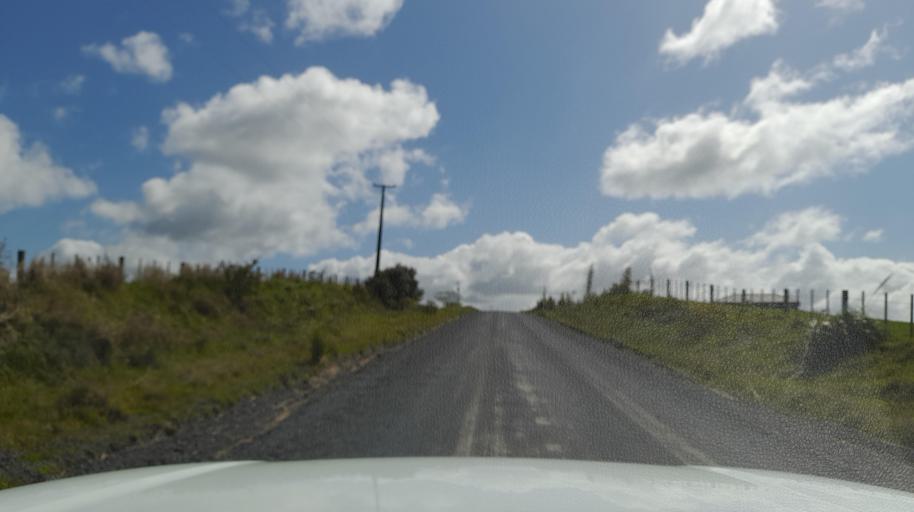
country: NZ
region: Northland
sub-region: Far North District
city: Kerikeri
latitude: -35.2222
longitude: 173.8721
